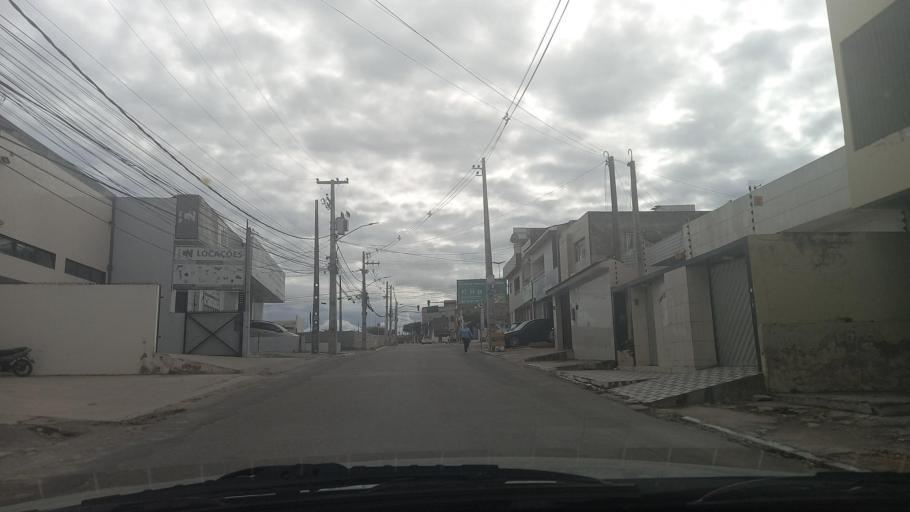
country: BR
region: Pernambuco
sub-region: Caruaru
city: Caruaru
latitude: -8.2864
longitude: -35.9952
